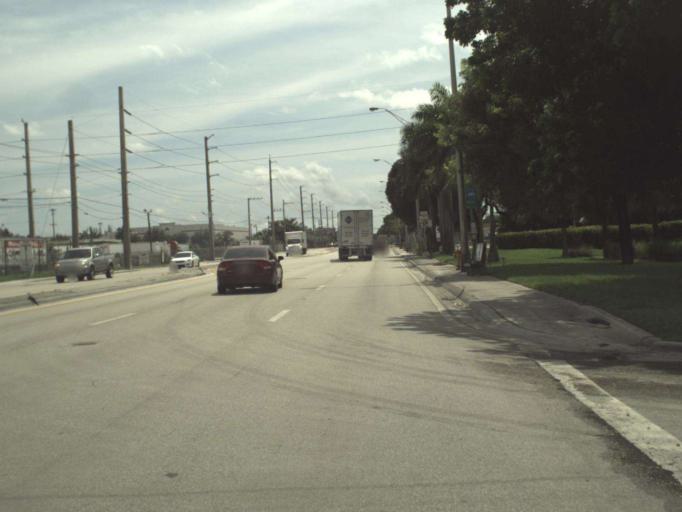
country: US
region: Florida
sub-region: Miami-Dade County
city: Virginia Gardens
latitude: 25.8290
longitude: -80.3139
